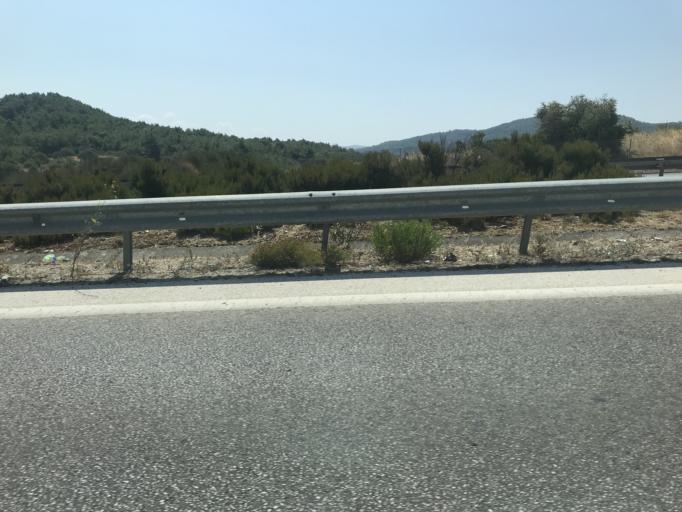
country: TR
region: Izmir
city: Urla
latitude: 38.3483
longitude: 26.8421
